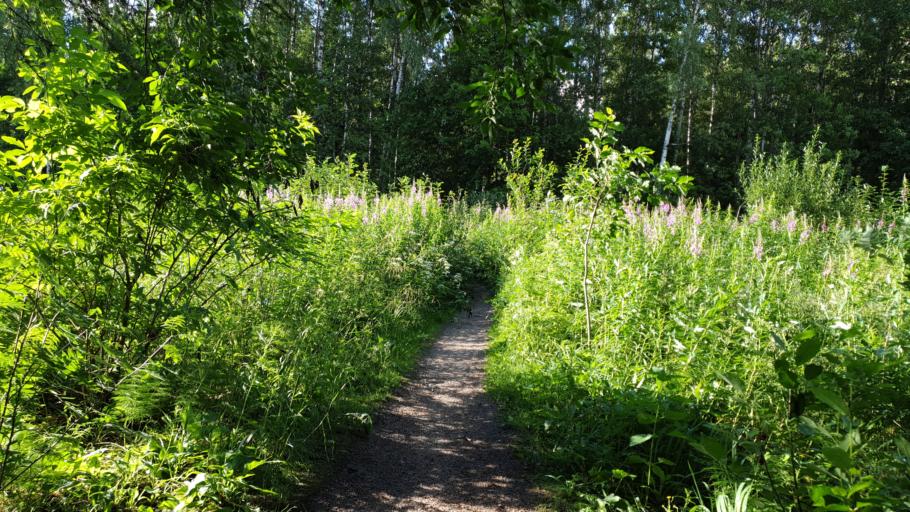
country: FI
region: Uusimaa
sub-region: Helsinki
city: Teekkarikylae
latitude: 60.2713
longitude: 24.9034
